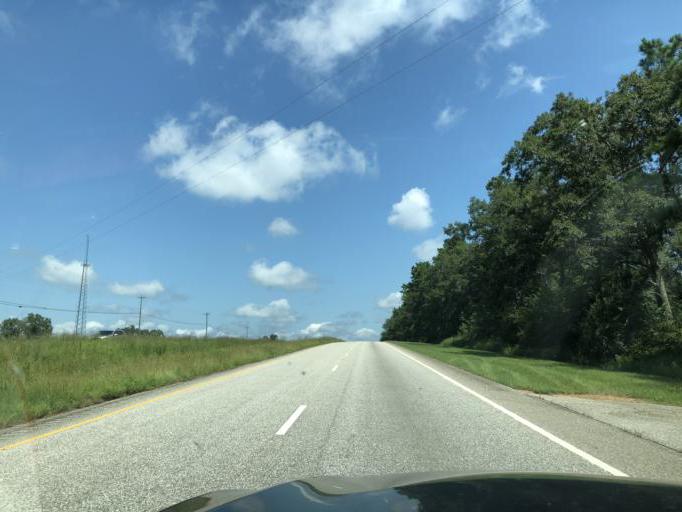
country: US
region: Alabama
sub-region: Henry County
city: Abbeville
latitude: 31.7091
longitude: -85.2743
